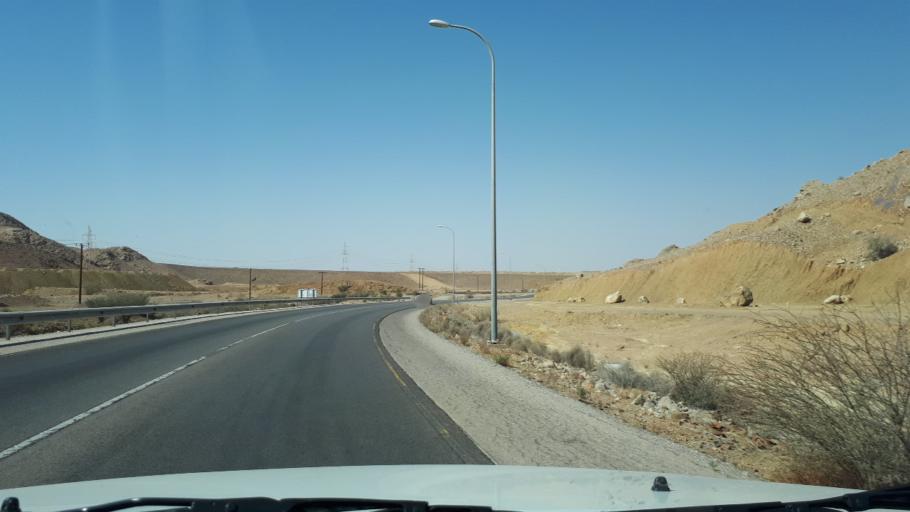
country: OM
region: Ash Sharqiyah
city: Sur
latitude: 22.3183
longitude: 59.3079
